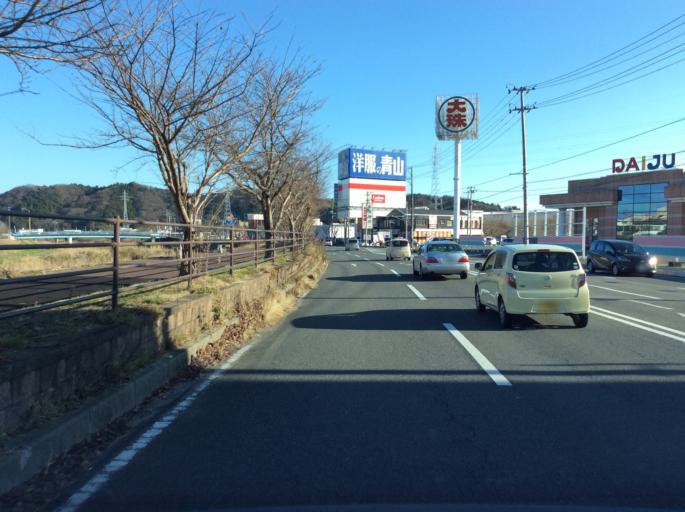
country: JP
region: Fukushima
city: Iwaki
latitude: 37.0476
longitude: 140.8980
